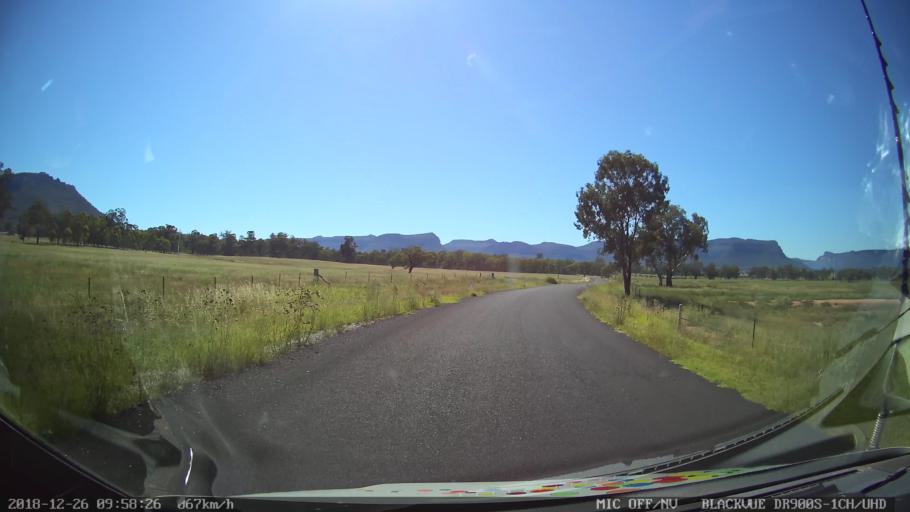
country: AU
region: New South Wales
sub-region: Mid-Western Regional
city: Kandos
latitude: -33.0387
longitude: 150.2048
